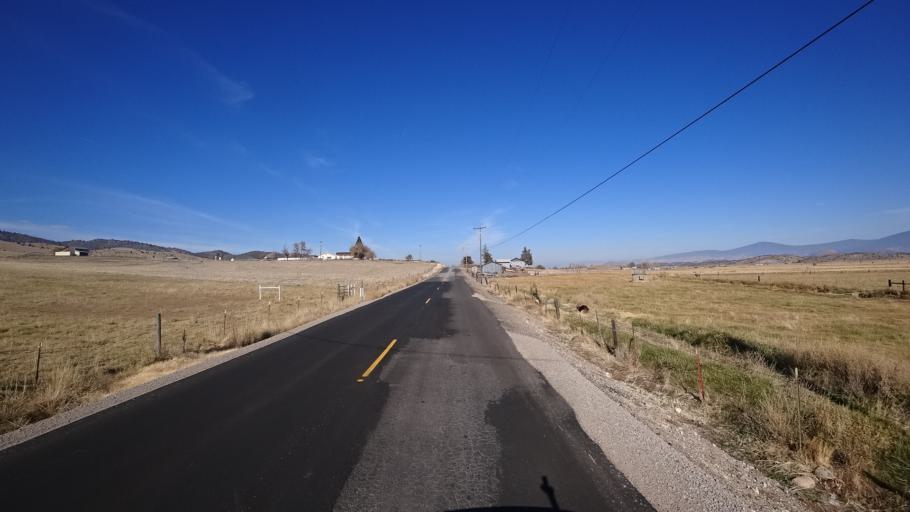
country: US
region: California
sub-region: Siskiyou County
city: Montague
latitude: 41.6058
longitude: -122.5302
